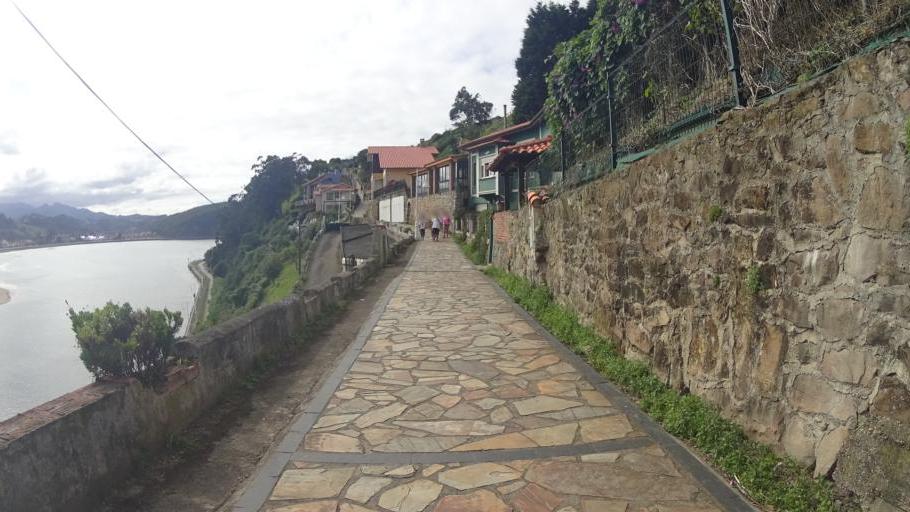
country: ES
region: Asturias
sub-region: Province of Asturias
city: Ribadesella
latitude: 43.4674
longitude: -5.0611
